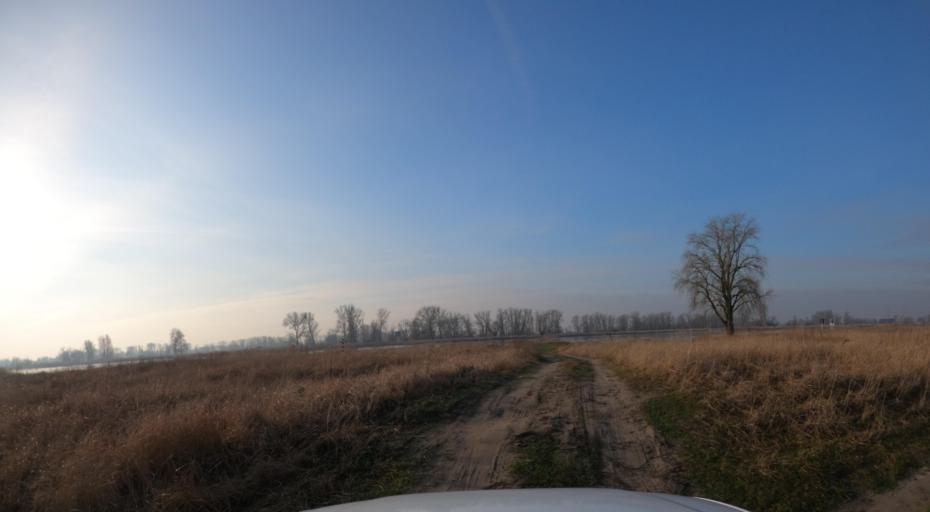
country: PL
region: Lubusz
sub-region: Powiat gorzowski
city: Kostrzyn nad Odra
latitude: 52.6022
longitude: 14.6082
